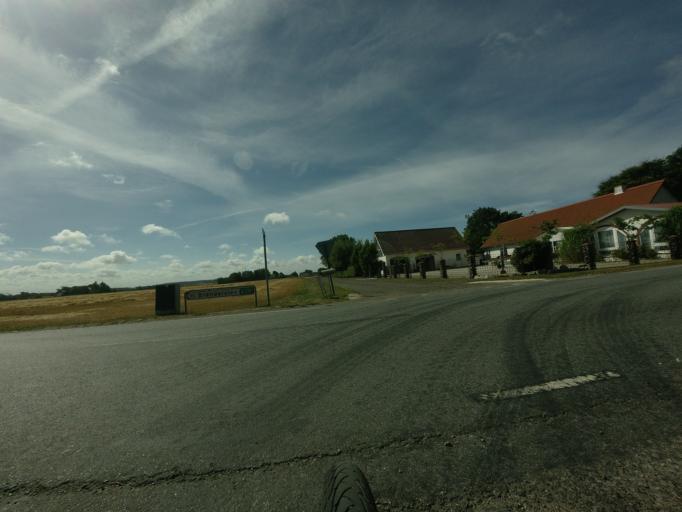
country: DK
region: North Denmark
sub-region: Hjorring Kommune
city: Vra
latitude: 57.3327
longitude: 9.8088
